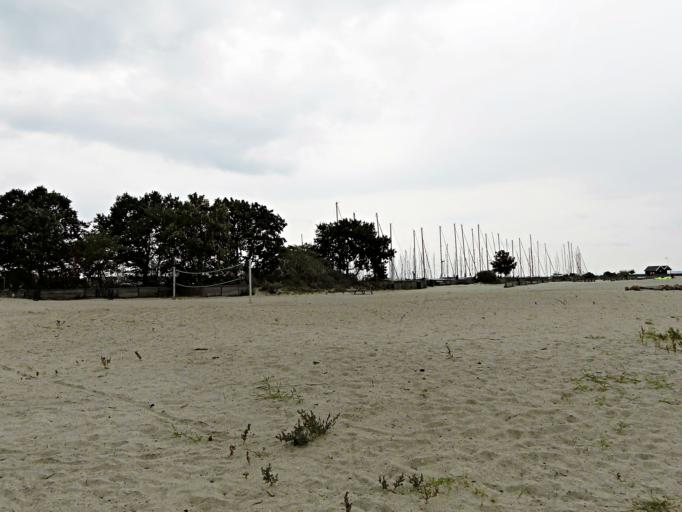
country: DK
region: Capital Region
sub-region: Rudersdal Kommune
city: Trorod
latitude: 55.8823
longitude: 12.5454
